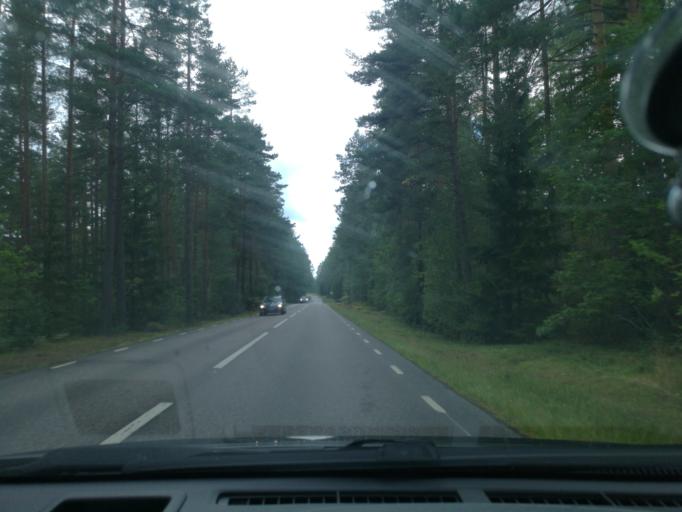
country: SE
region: OEstergoetland
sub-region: Motala Kommun
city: Borensberg
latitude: 58.6648
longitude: 15.3110
